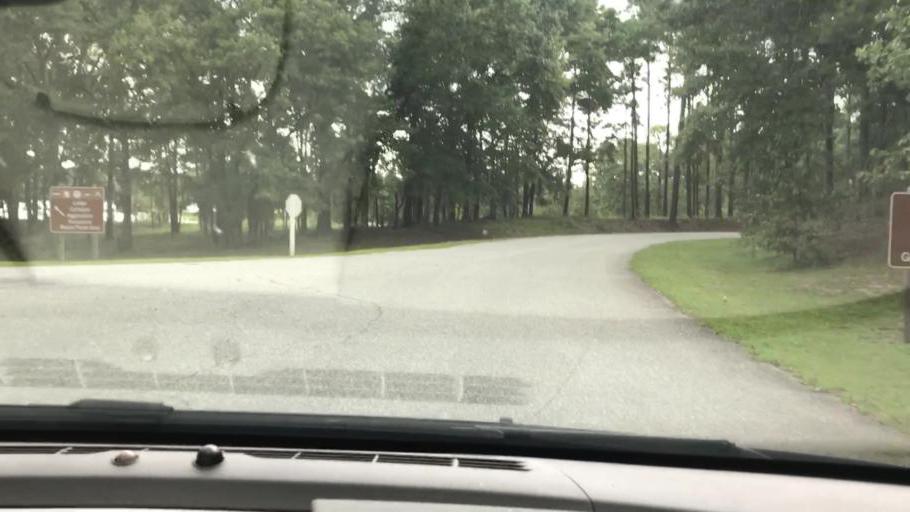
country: US
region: Georgia
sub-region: Clay County
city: Fort Gaines
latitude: 31.6663
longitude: -85.0562
